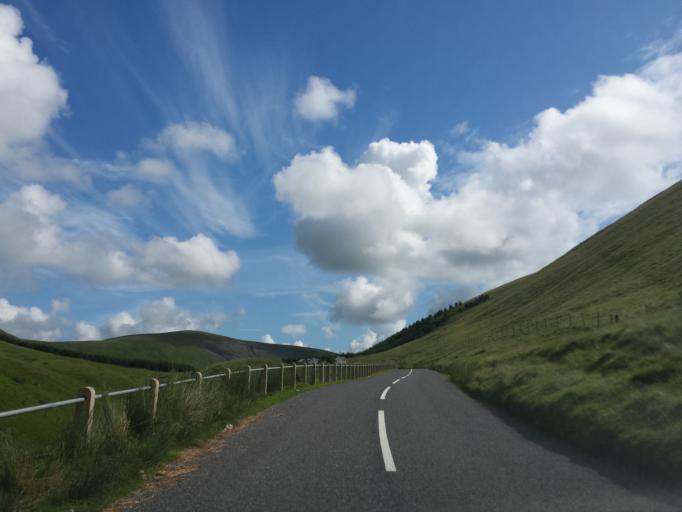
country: GB
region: Scotland
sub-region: Dumfries and Galloway
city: Moffat
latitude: 55.4276
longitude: -3.2681
